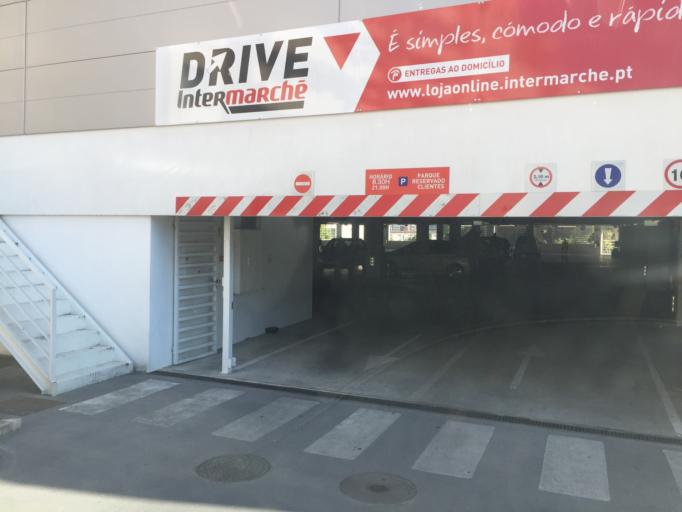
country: PT
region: Lisbon
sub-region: Odivelas
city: Povoa de Santo Adriao
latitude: 38.8156
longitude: -9.1587
